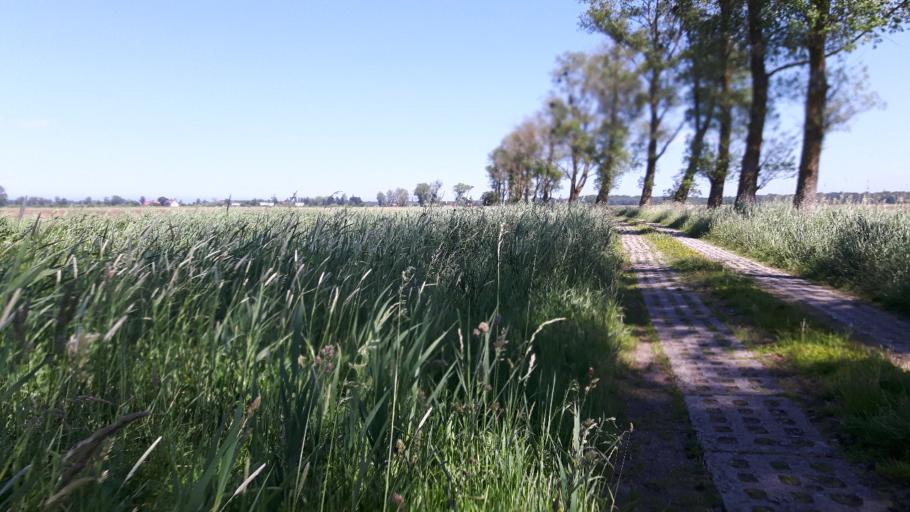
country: PL
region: Pomeranian Voivodeship
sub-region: Powiat slupski
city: Smoldzino
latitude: 54.6779
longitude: 17.2681
